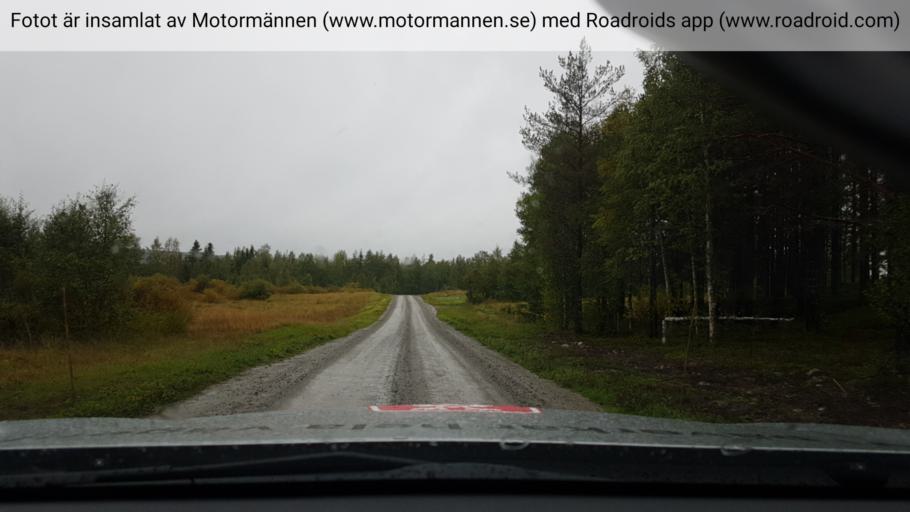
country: SE
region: Vaesterbotten
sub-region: Asele Kommun
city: Asele
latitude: 64.0770
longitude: 17.5710
